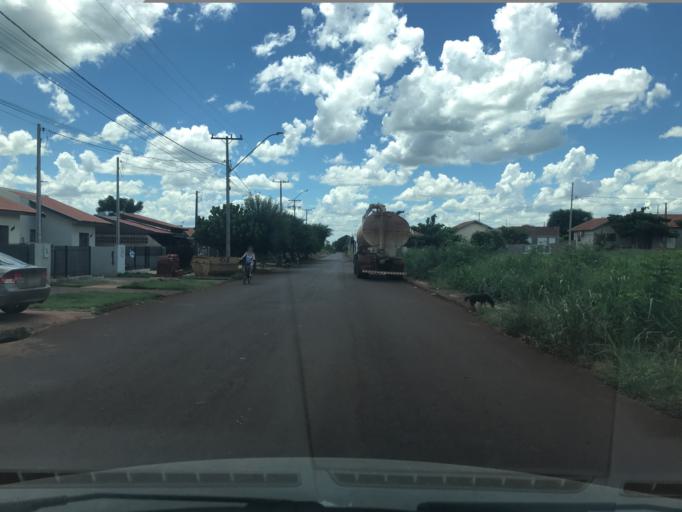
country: BR
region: Parana
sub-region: Palotina
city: Palotina
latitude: -24.2682
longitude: -53.8485
